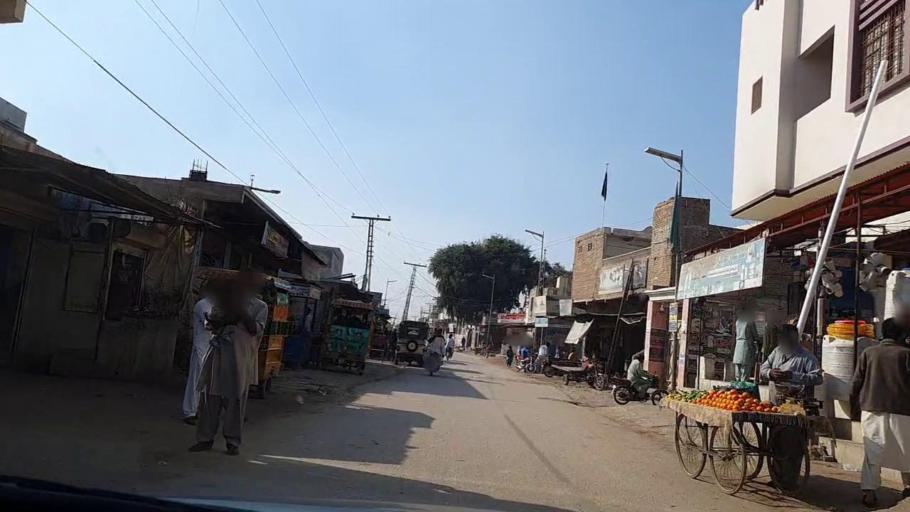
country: PK
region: Sindh
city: Sakrand
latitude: 26.1367
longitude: 68.2687
